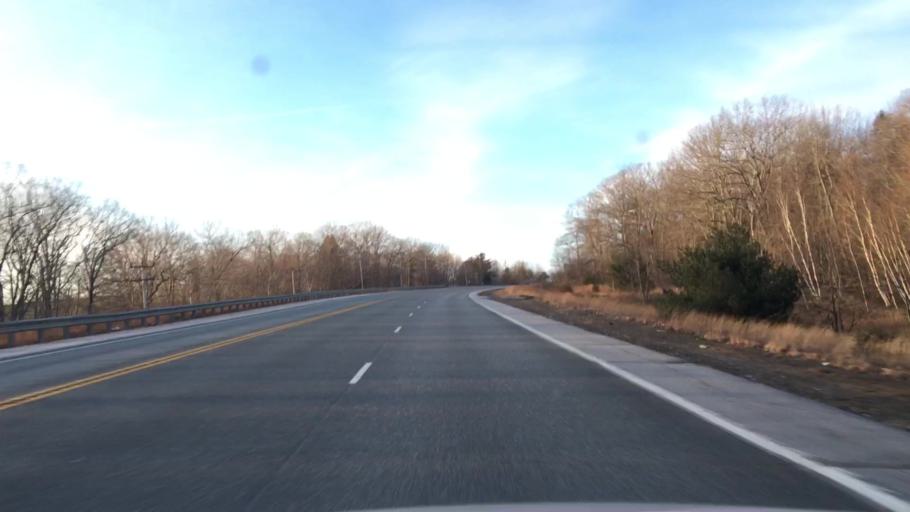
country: US
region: Maine
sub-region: Hancock County
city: Dedham
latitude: 44.6965
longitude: -68.5941
